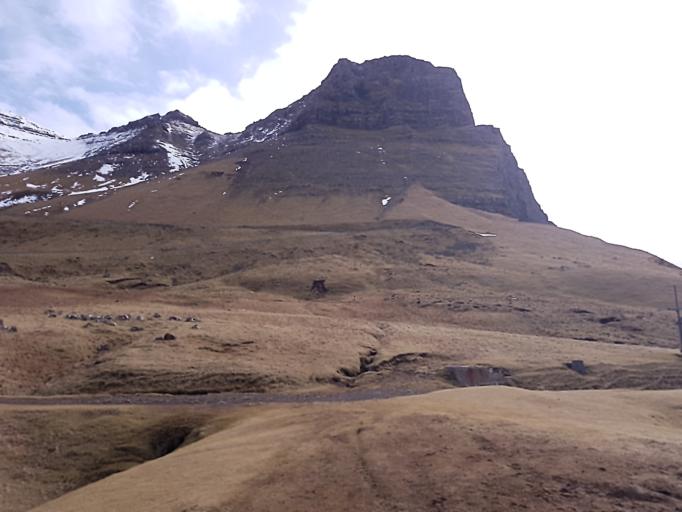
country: FO
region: Vagar
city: Sorvagur
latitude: 62.1066
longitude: -7.4348
